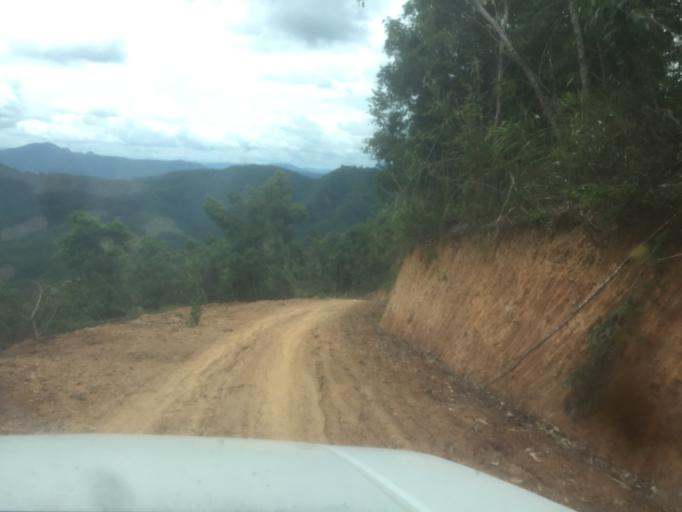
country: LA
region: Phongsali
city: Khoa
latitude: 20.9252
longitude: 102.5517
